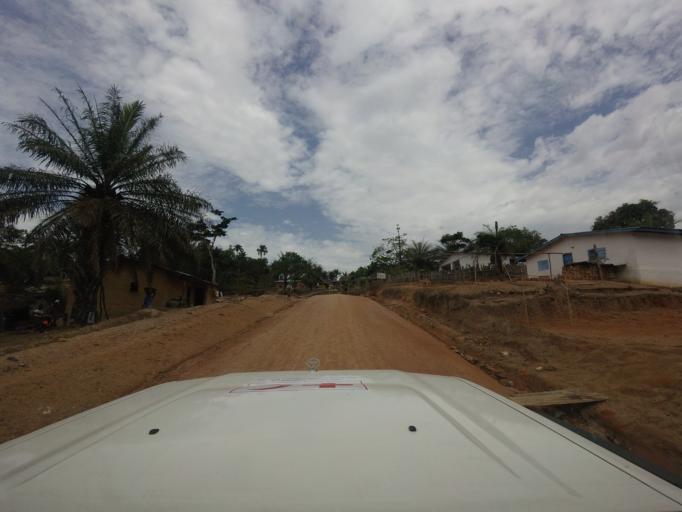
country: SL
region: Eastern Province
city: Buedu
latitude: 8.2334
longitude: -10.2244
